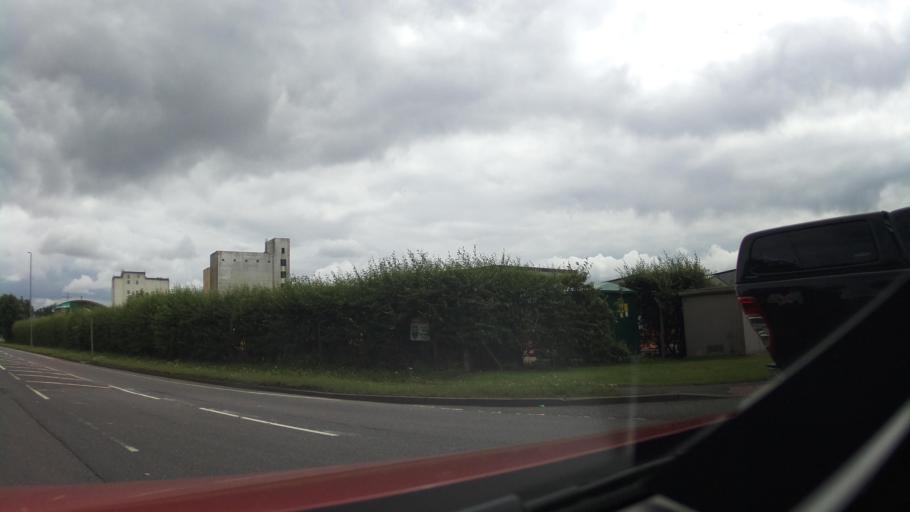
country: GB
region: England
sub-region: Northamptonshire
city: Corby
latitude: 52.5112
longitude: -0.6900
